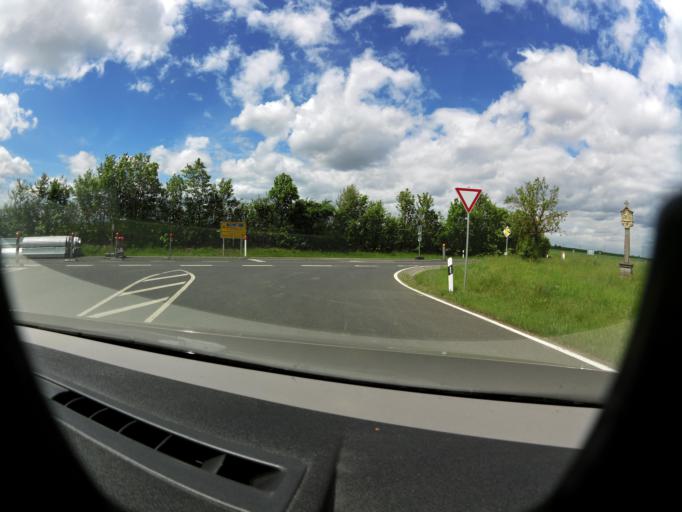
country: DE
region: Bavaria
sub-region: Regierungsbezirk Unterfranken
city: Frickenhausen
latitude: 49.7112
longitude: 10.0802
